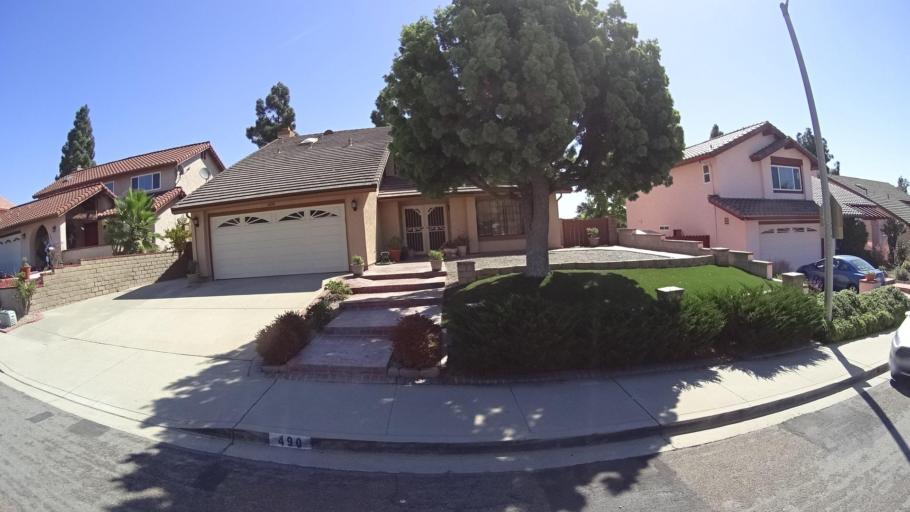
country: US
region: California
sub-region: San Diego County
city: Bonita
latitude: 32.6442
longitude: -117.0454
